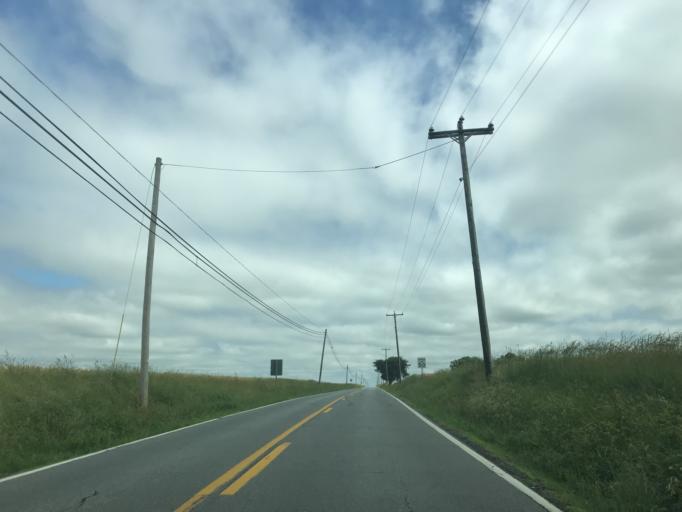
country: US
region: Maryland
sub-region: Caroline County
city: Ridgely
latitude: 38.8929
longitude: -75.9600
